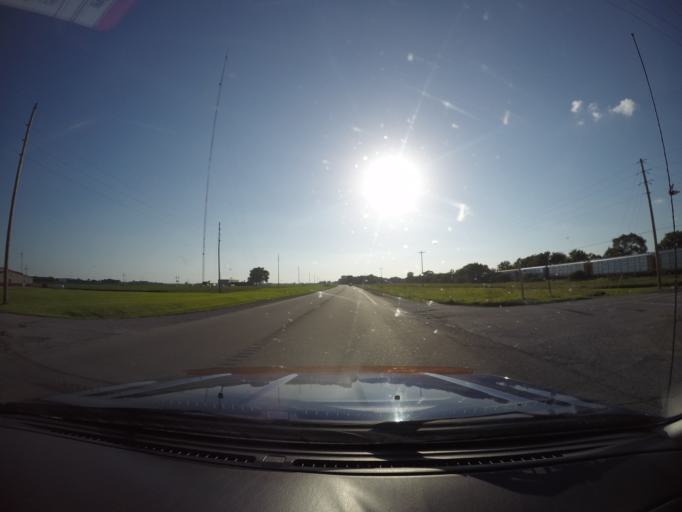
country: US
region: Kansas
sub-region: Shawnee County
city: Silver Lake
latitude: 39.0941
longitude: -95.7808
